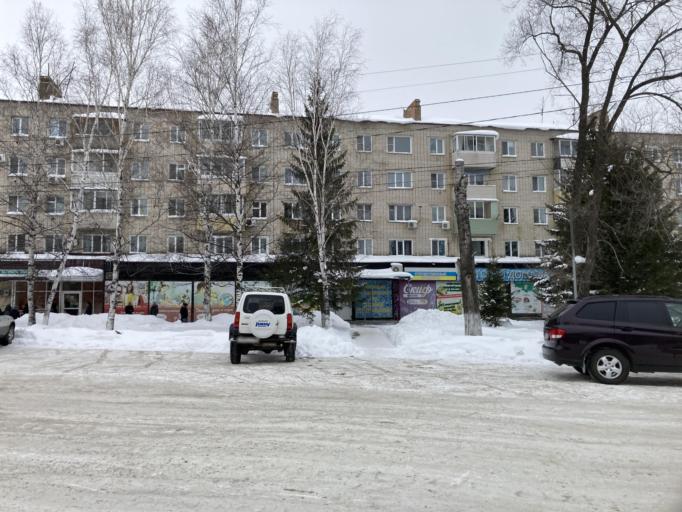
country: RU
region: Khabarovsk Krai
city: Khor
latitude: 47.9700
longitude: 135.0520
